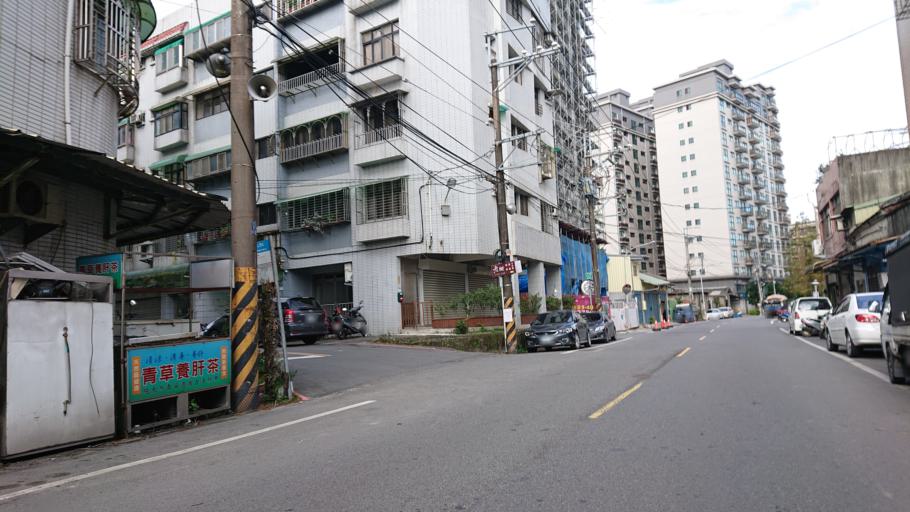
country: TW
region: Taiwan
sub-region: Taoyuan
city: Taoyuan
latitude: 24.9259
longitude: 121.3667
